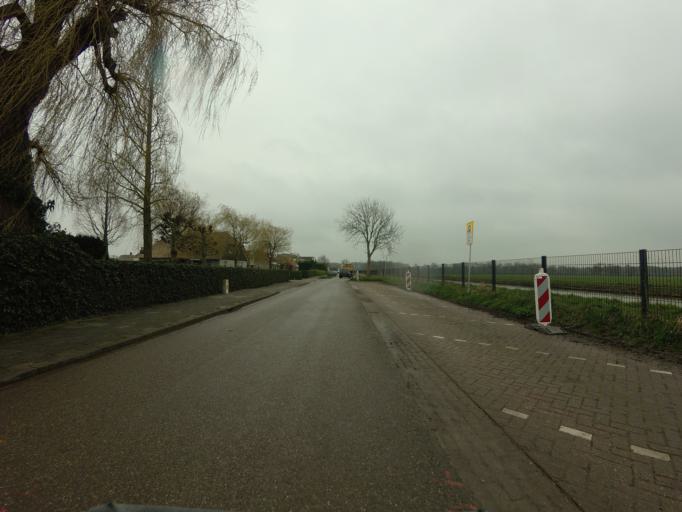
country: NL
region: Utrecht
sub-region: Stichtse Vecht
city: Breukelen
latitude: 52.1812
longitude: 5.0195
